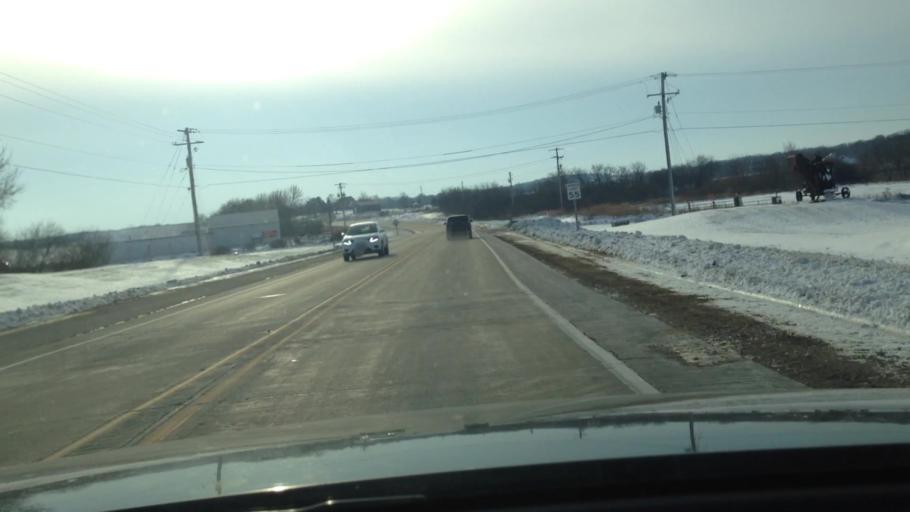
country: US
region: Wisconsin
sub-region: Walworth County
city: Lake Geneva
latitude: 42.5609
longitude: -88.4167
